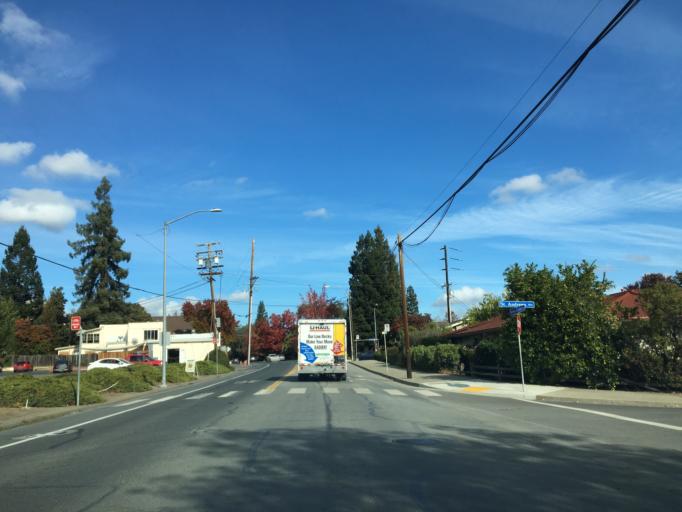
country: US
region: California
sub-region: Santa Clara County
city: Cupertino
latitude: 37.3131
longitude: -122.0688
